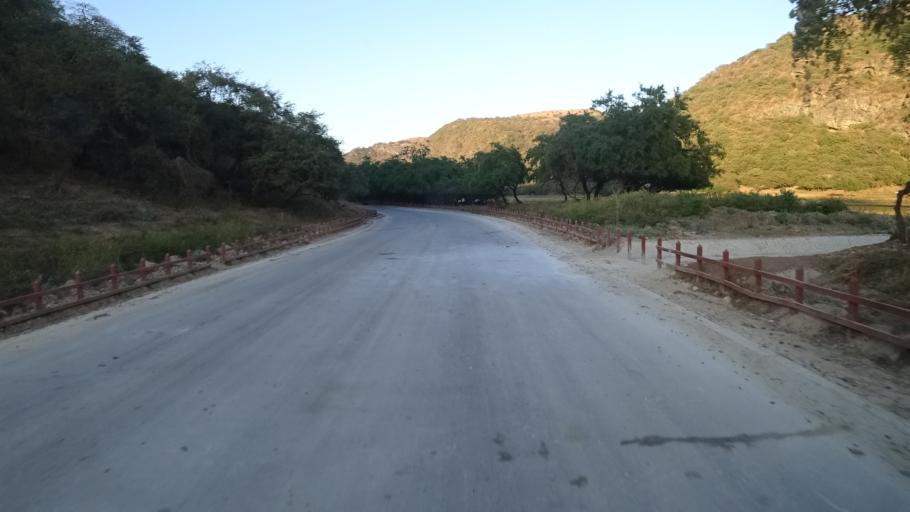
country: OM
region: Zufar
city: Salalah
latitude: 17.0941
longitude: 54.4481
